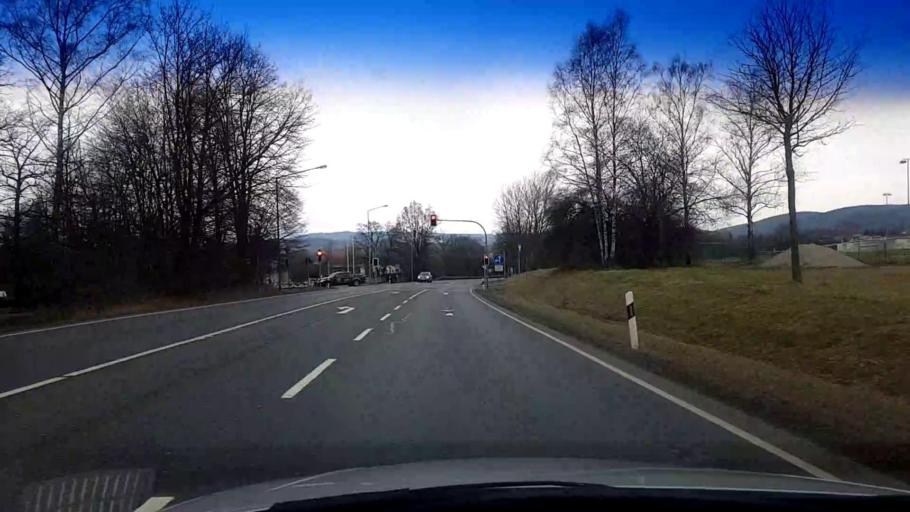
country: DE
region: Bavaria
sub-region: Upper Franconia
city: Kulmbach
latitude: 50.0882
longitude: 11.4552
